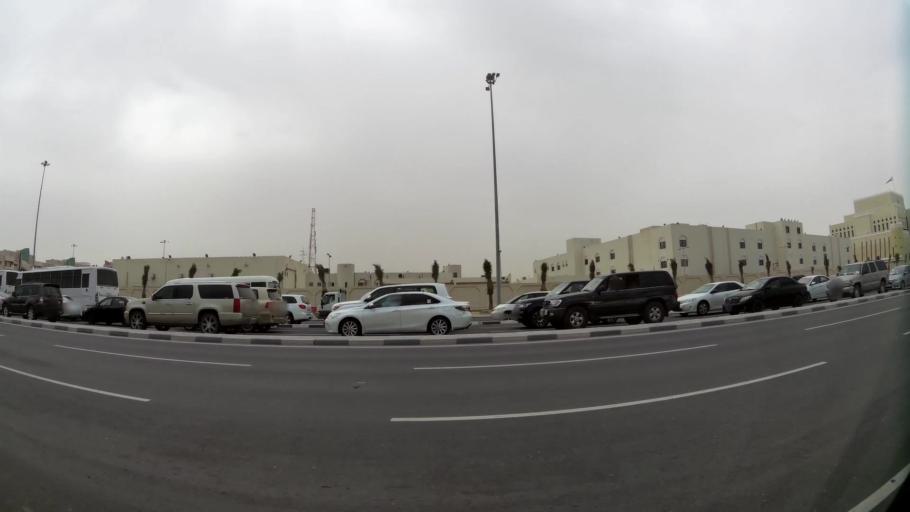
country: QA
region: Baladiyat ad Dawhah
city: Doha
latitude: 25.3030
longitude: 51.5070
